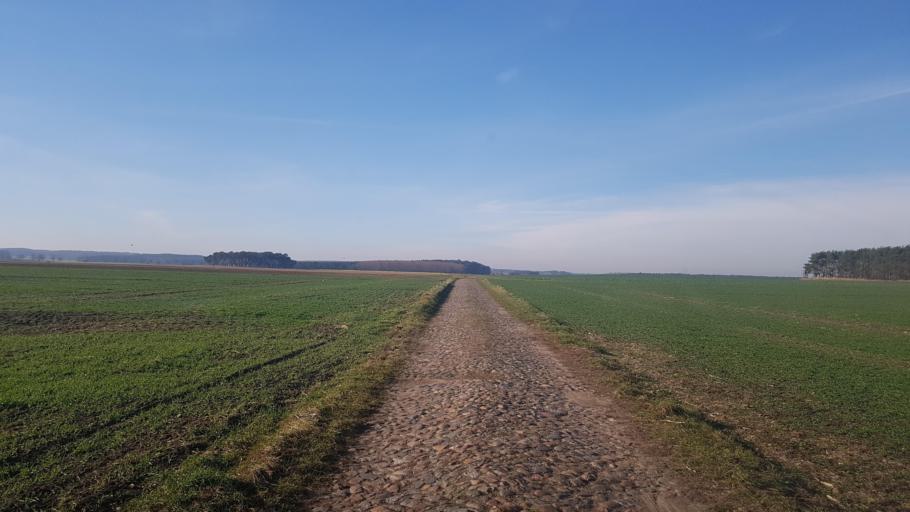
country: DE
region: Brandenburg
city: Niemegk
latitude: 52.1193
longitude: 12.6657
